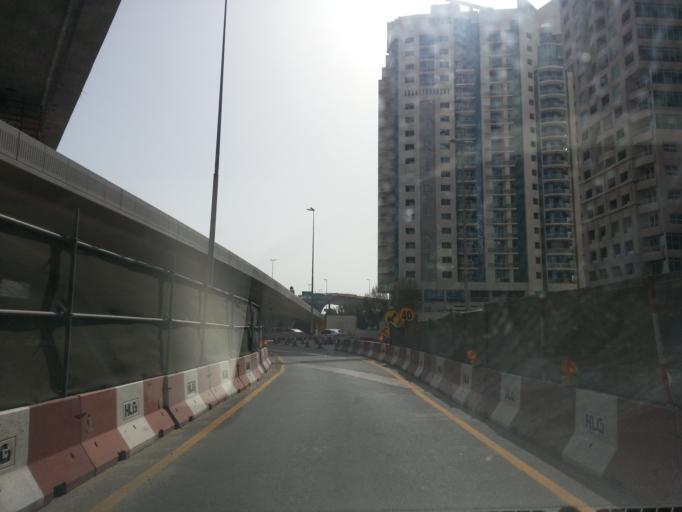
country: AE
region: Dubai
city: Dubai
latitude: 25.0675
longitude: 55.1331
